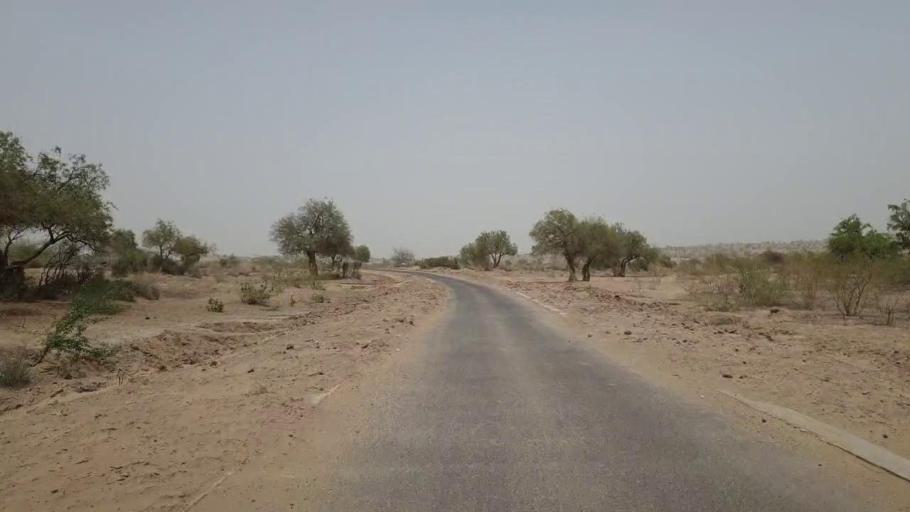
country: PK
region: Sindh
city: Islamkot
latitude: 24.7963
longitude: 70.5428
